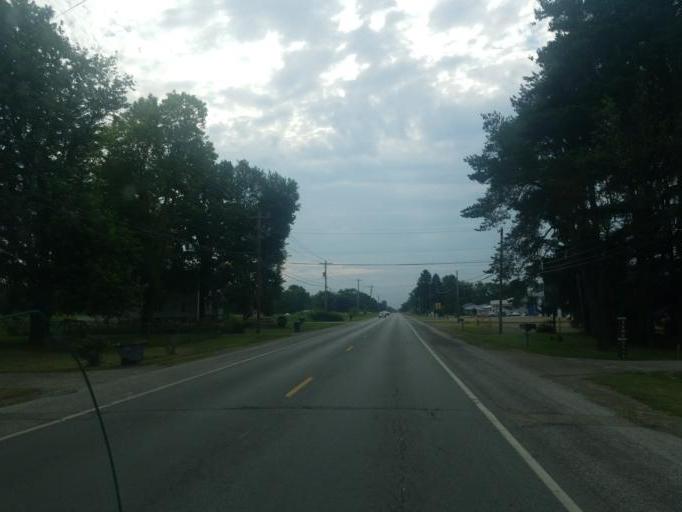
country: US
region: Ohio
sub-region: Wayne County
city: Apple Creek
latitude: 40.7972
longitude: -81.8395
